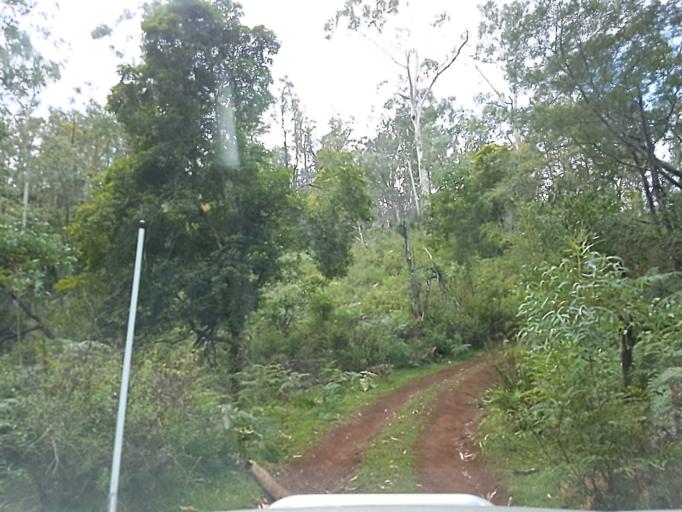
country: AU
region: Victoria
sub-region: East Gippsland
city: Lakes Entrance
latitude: -37.3617
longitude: 148.3540
